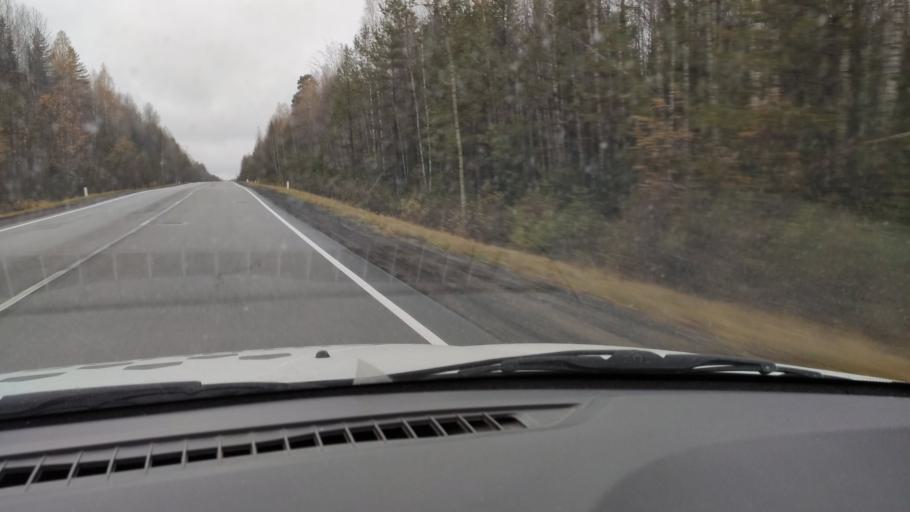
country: RU
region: Kirov
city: Chernaya Kholunitsa
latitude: 58.8688
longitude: 51.5561
